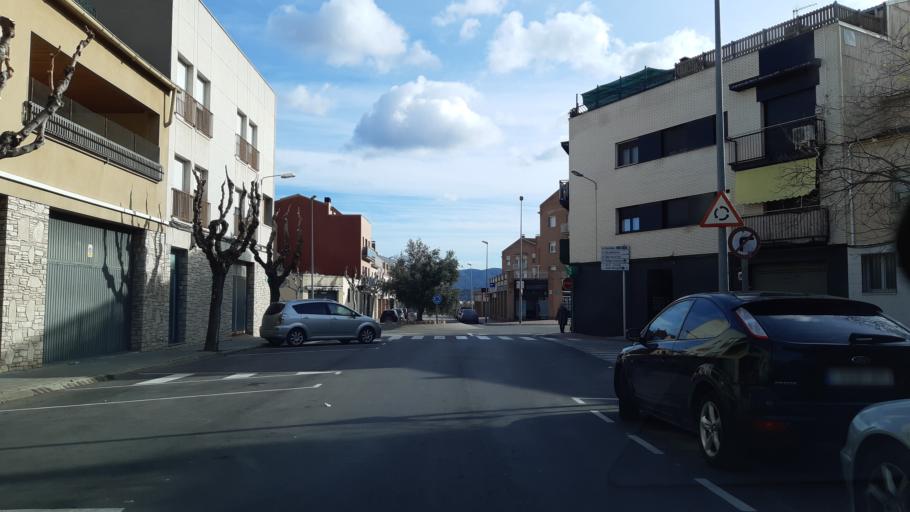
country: ES
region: Catalonia
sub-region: Provincia de Barcelona
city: Vilanova del Cami
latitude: 41.5696
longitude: 1.6420
